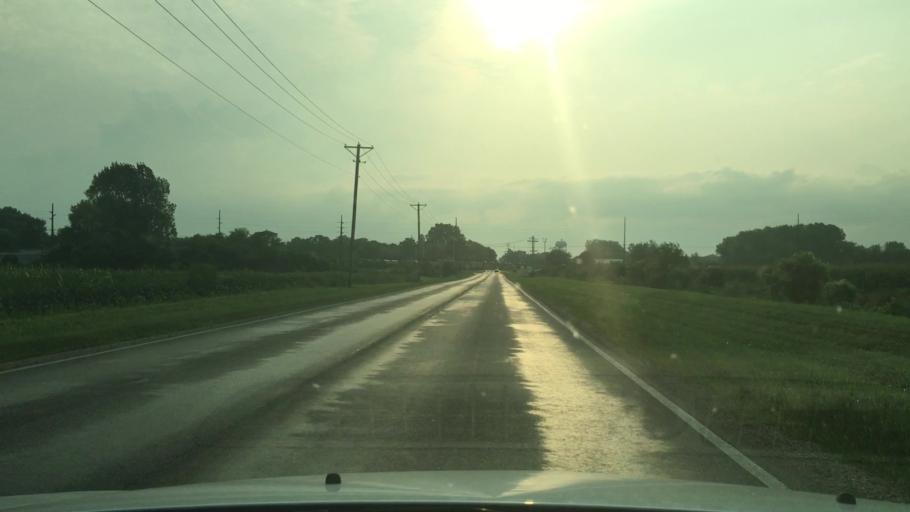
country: US
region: Illinois
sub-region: Ogle County
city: Rochelle
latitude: 41.9198
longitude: -89.0509
